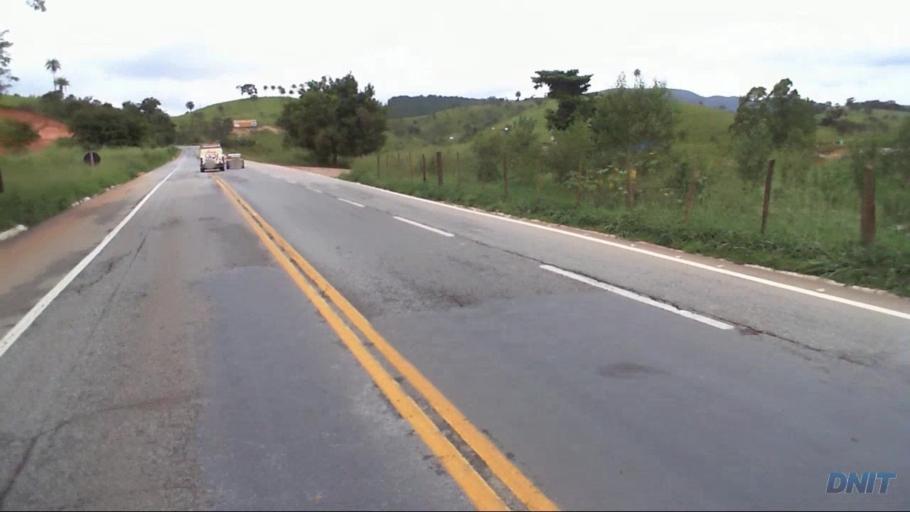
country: BR
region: Minas Gerais
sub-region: Barao De Cocais
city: Barao de Cocais
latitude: -19.8166
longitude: -43.3957
